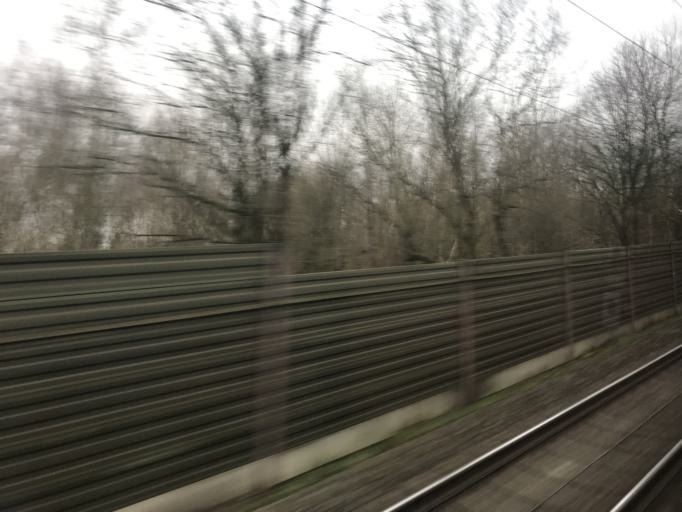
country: DE
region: Lower Saxony
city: Uetze
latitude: 52.4295
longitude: 10.2290
